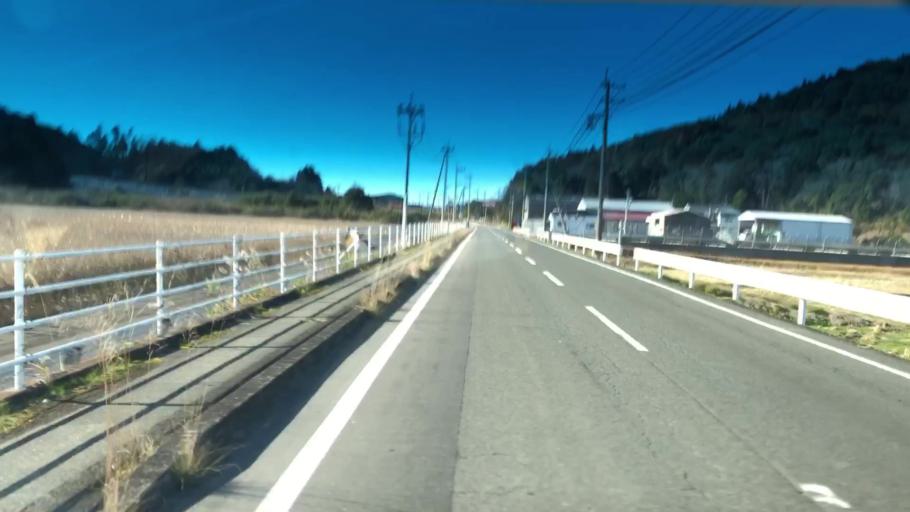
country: JP
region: Kagoshima
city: Satsumasendai
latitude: 31.8184
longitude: 130.2677
